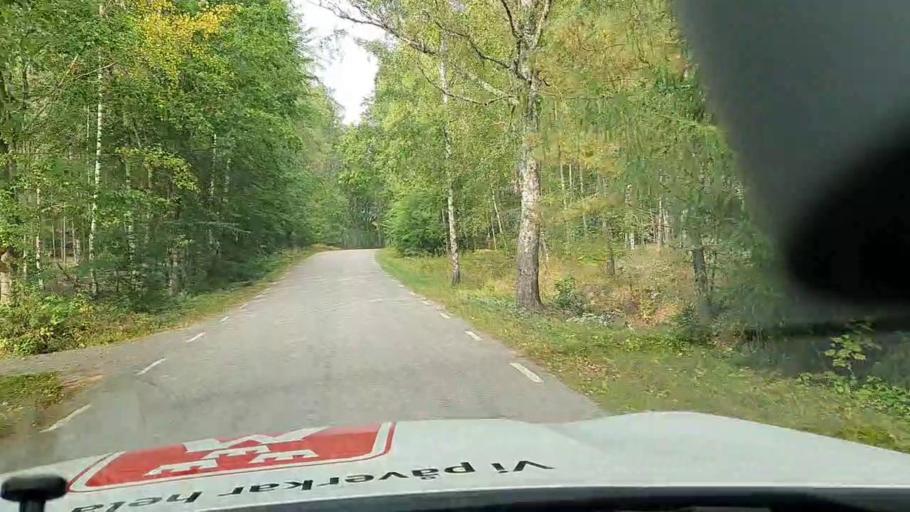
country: SE
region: Soedermanland
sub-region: Nykopings Kommun
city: Svalsta
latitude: 58.8300
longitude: 16.8822
